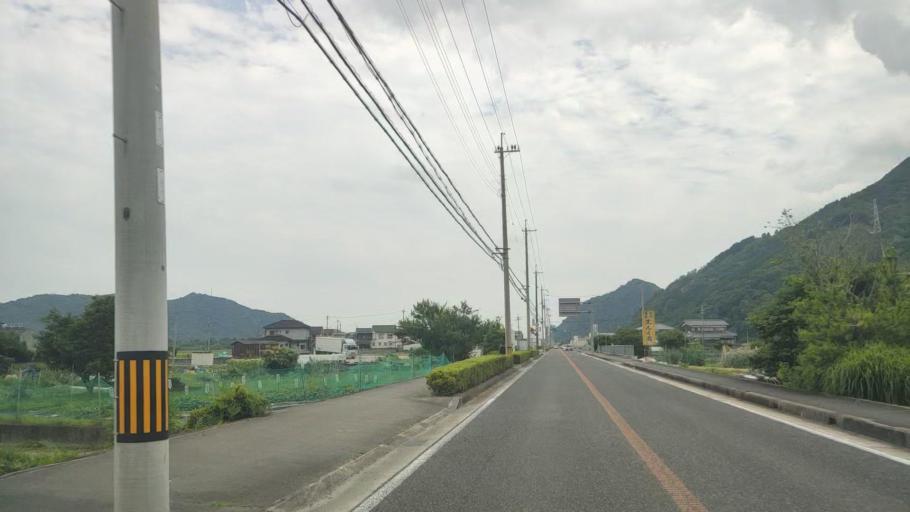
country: JP
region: Hyogo
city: Tatsunocho-tominaga
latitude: 34.8919
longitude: 134.5464
